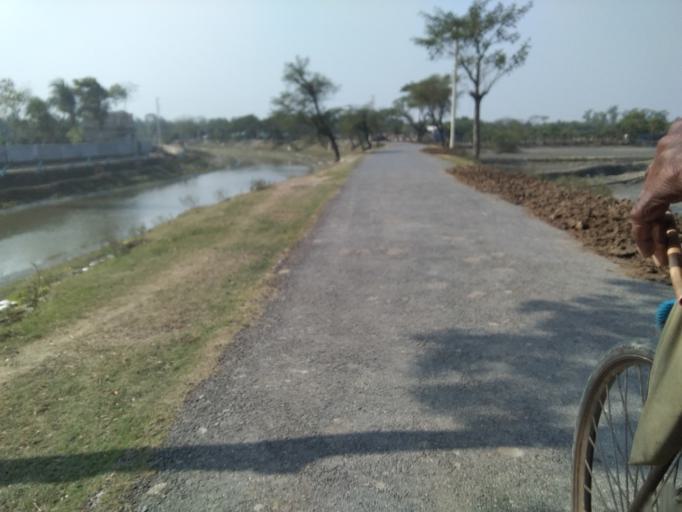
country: IN
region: West Bengal
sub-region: North 24 Parganas
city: Taki
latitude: 22.6364
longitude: 89.0042
